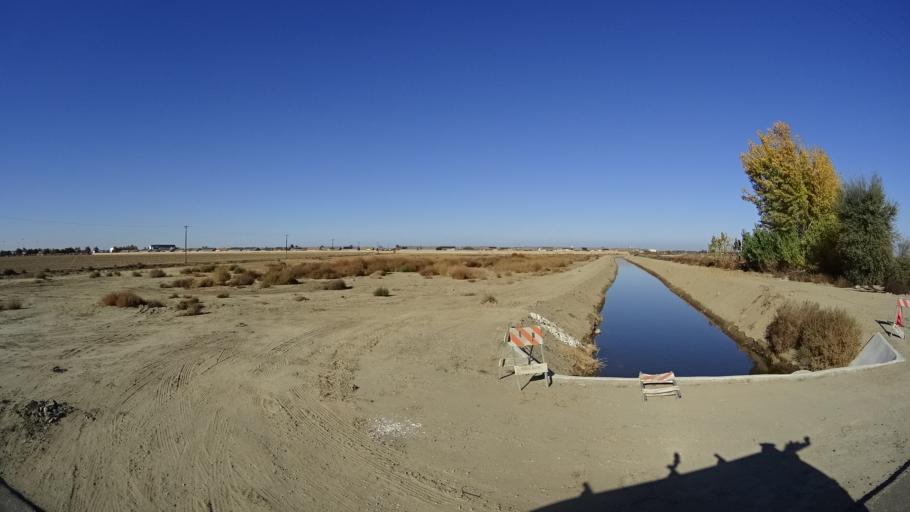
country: US
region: California
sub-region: Kern County
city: Greenacres
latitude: 35.2819
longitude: -119.1049
